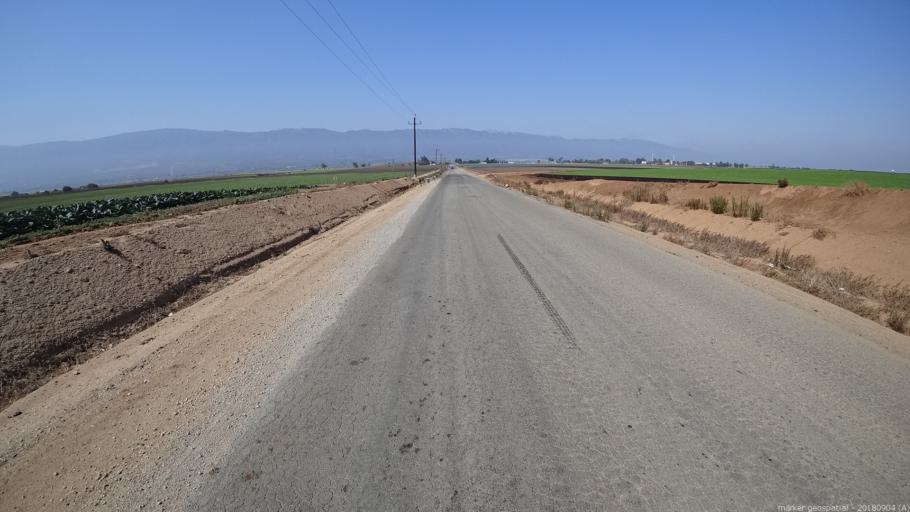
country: US
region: California
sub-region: Monterey County
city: Gonzales
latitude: 36.4967
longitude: -121.4169
